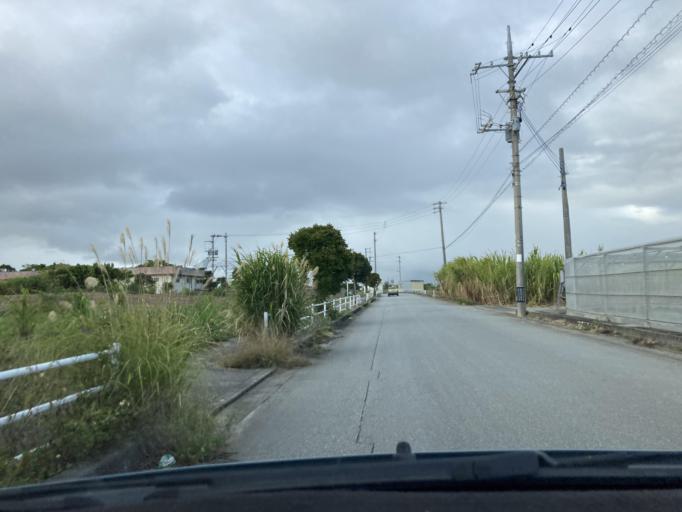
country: JP
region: Okinawa
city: Itoman
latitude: 26.1256
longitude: 127.6866
